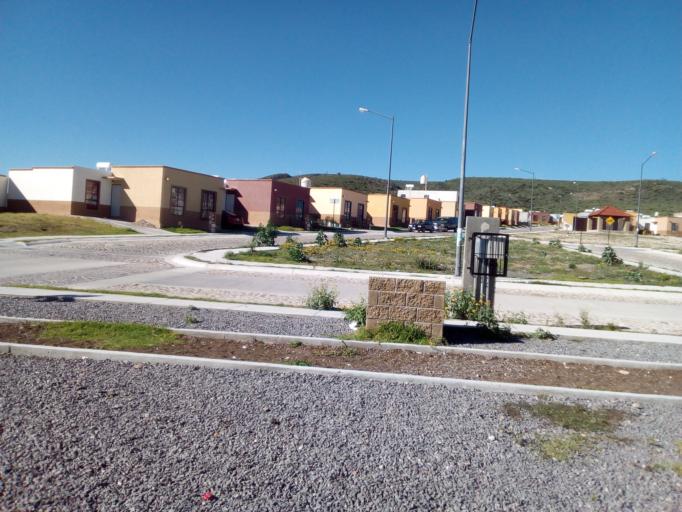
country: MX
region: Guanajuato
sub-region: San Luis de la Paz
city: San Luis de la Paz
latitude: 21.3079
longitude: -100.5085
